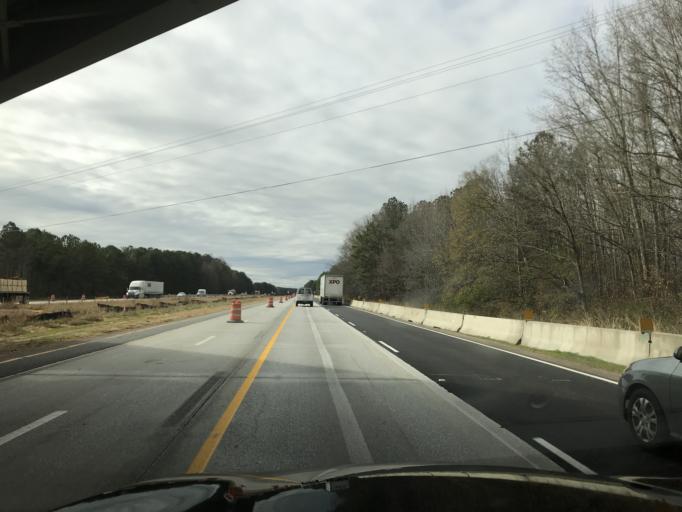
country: US
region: Georgia
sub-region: Carroll County
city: Villa Rica
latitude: 33.7176
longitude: -84.9757
